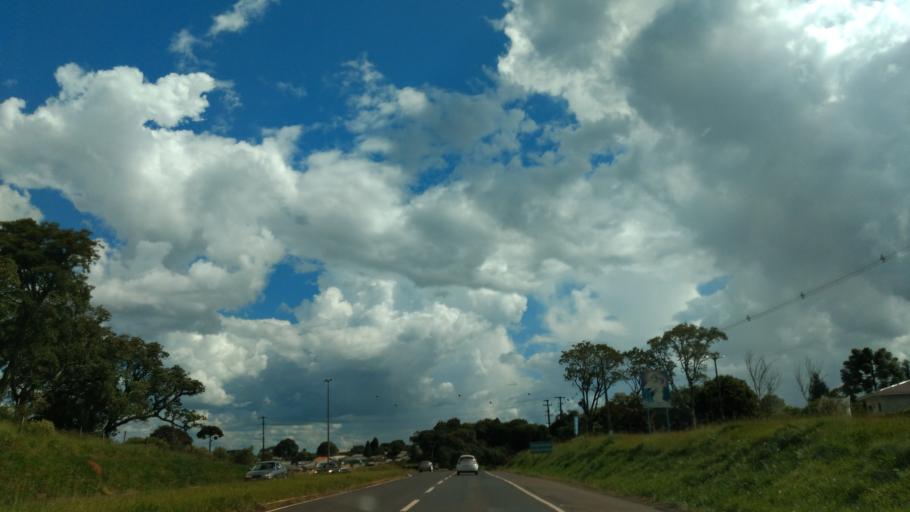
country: BR
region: Parana
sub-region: Guarapuava
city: Guarapuava
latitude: -25.4277
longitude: -51.4925
